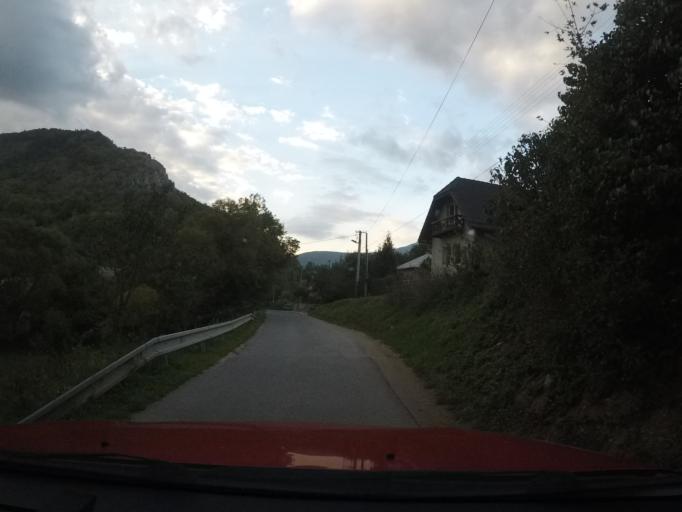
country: SK
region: Kosicky
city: Roznava
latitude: 48.6378
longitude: 20.6994
